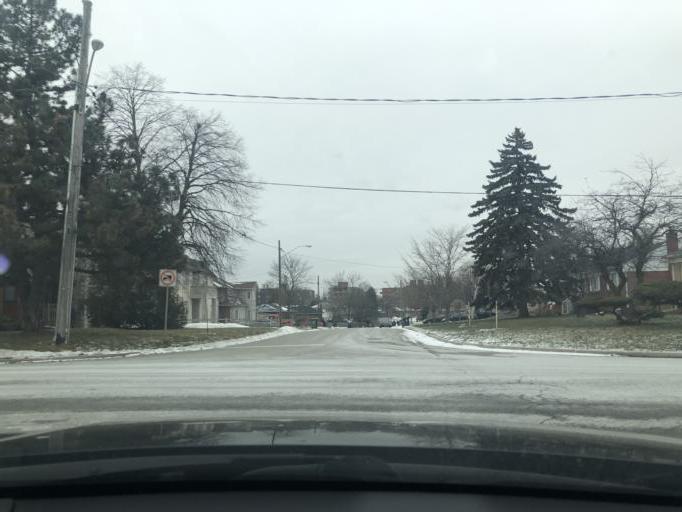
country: CA
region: Ontario
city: Scarborough
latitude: 43.7811
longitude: -79.2929
